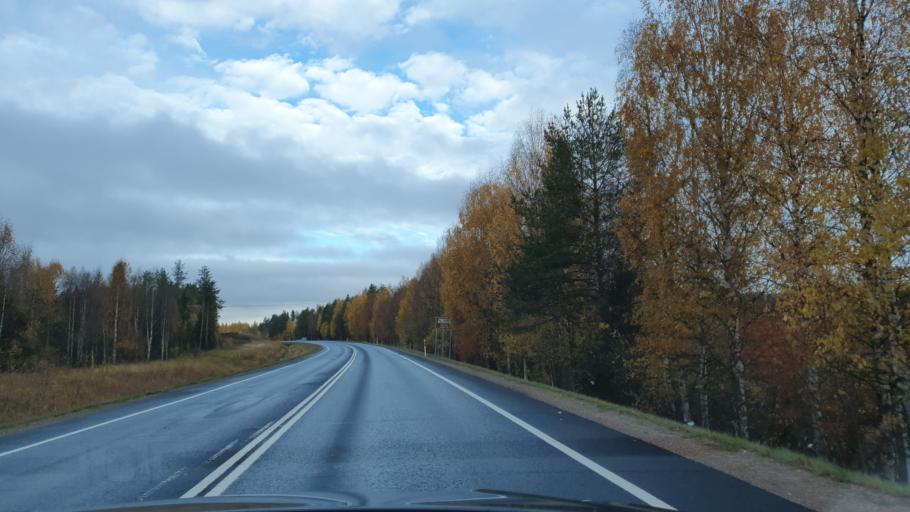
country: FI
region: Lapland
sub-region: Rovaniemi
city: Rovaniemi
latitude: 66.5982
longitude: 25.5938
